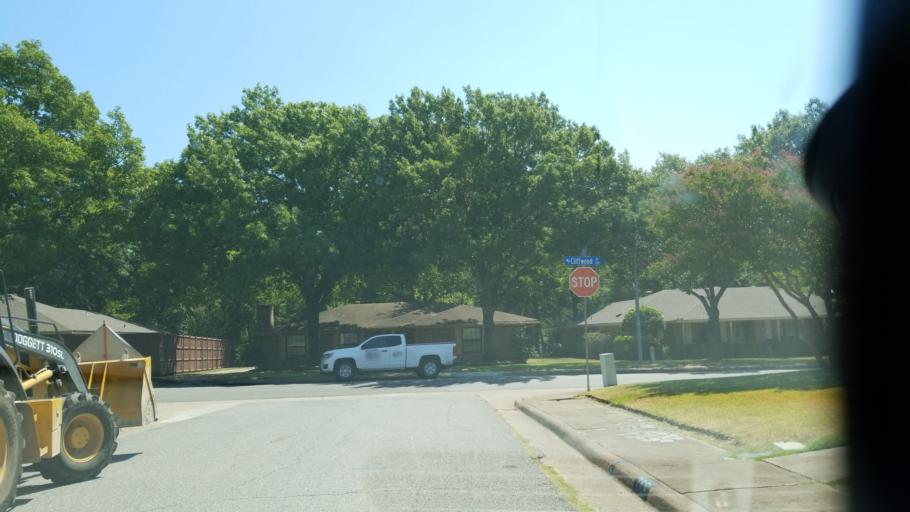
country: US
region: Texas
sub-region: Dallas County
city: Duncanville
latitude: 32.6488
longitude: -96.8946
